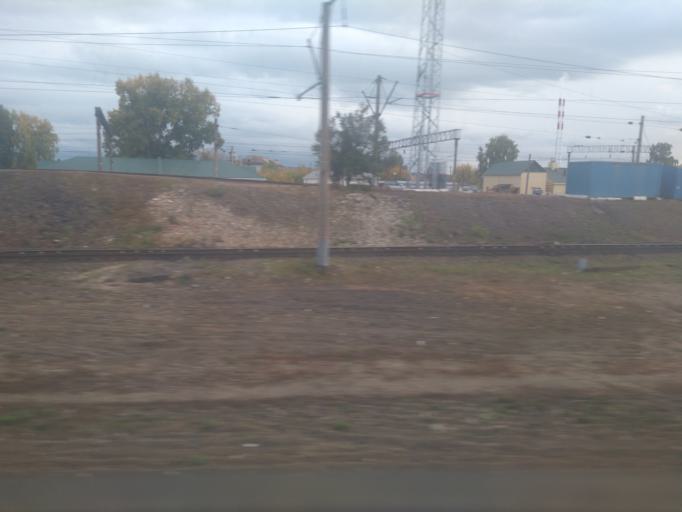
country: RU
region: Tatarstan
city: Staroye Arakchino
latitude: 55.8162
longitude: 48.9061
